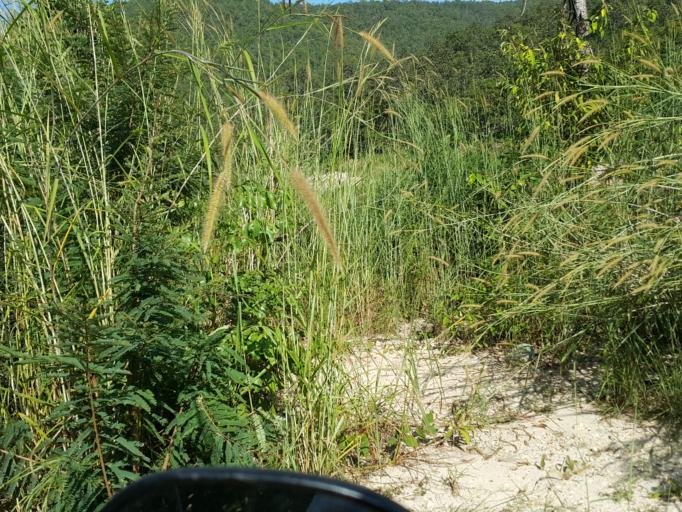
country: TH
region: Chiang Mai
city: Mae On
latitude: 18.7780
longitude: 99.2092
